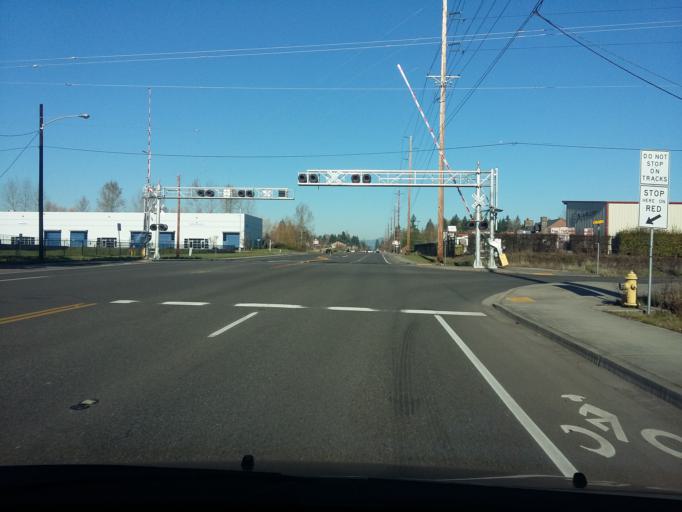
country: US
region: Washington
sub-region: Clark County
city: Barberton
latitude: 45.6928
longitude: -122.5992
